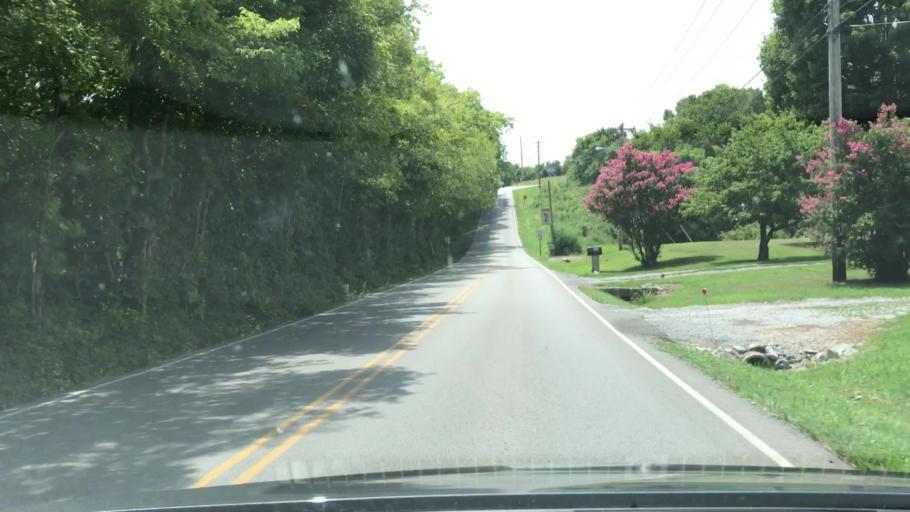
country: US
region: Tennessee
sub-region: Rutherford County
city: La Vergne
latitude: 35.9675
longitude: -86.6008
